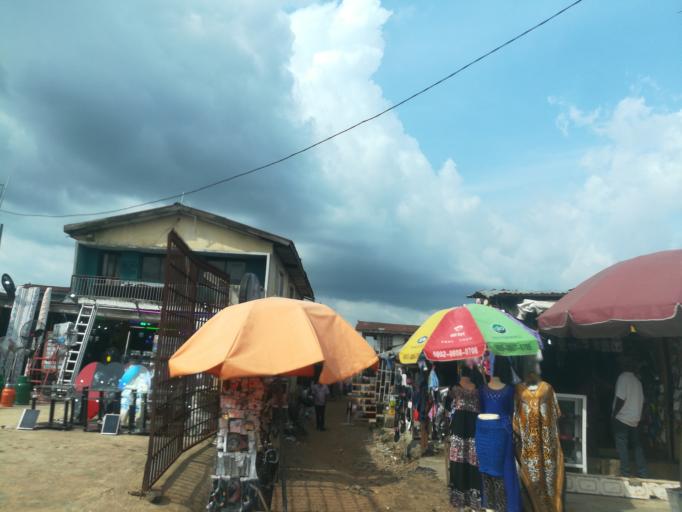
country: NG
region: Oyo
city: Ibadan
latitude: 7.3835
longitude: 3.8284
